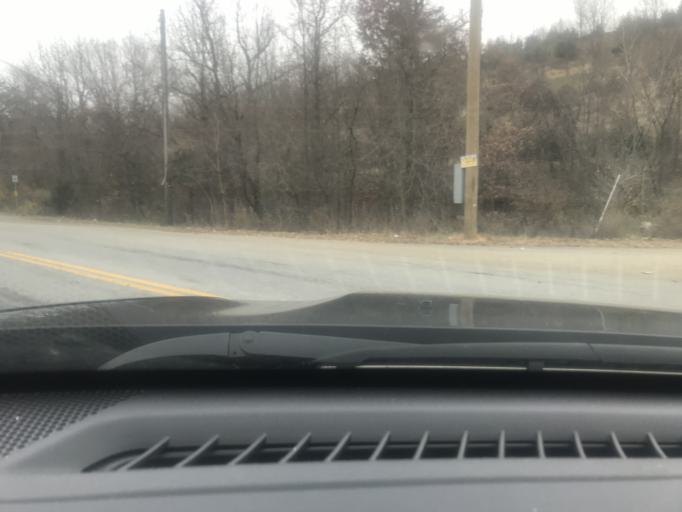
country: US
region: Maryland
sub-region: Prince George's County
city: Friendly
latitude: 38.7747
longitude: -76.9730
